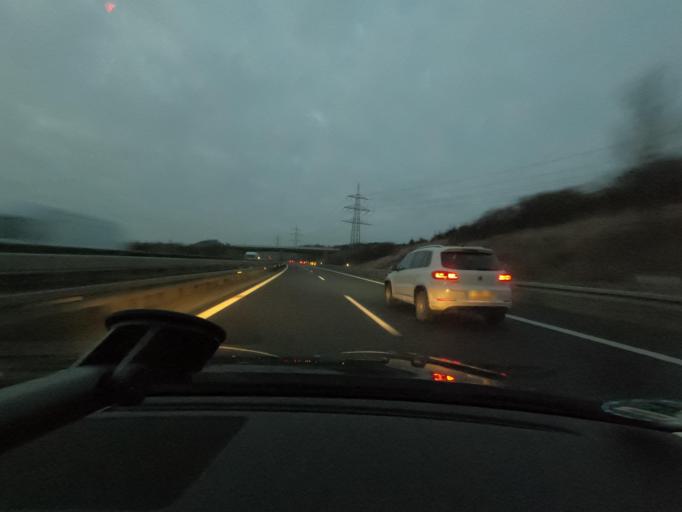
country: DE
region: Bavaria
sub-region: Upper Franconia
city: Rodental
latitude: 50.2434
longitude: 11.0447
